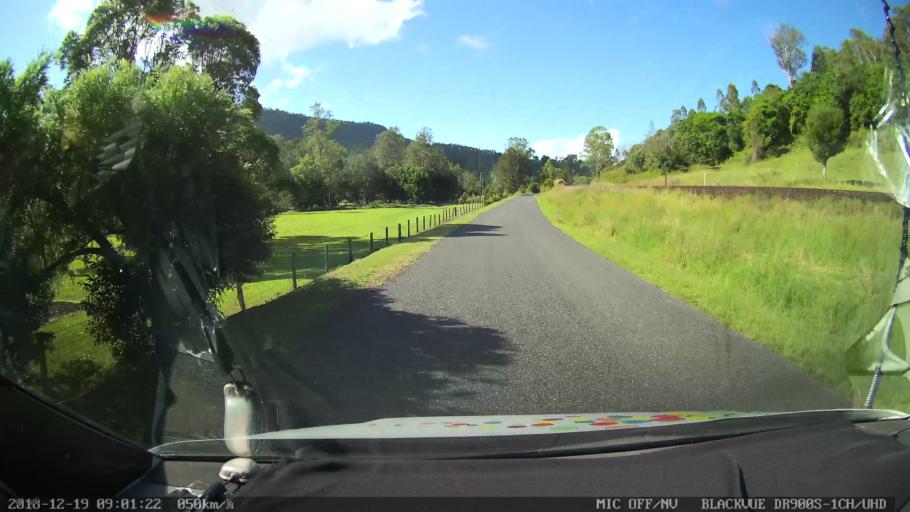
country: AU
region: New South Wales
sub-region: Kyogle
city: Kyogle
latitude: -28.4384
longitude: 152.9594
